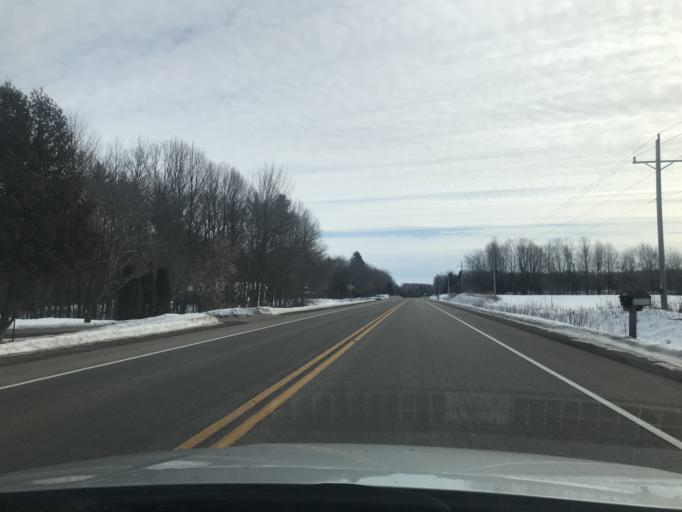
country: US
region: Wisconsin
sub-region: Oconto County
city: Oconto Falls
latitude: 44.8923
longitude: -88.1702
